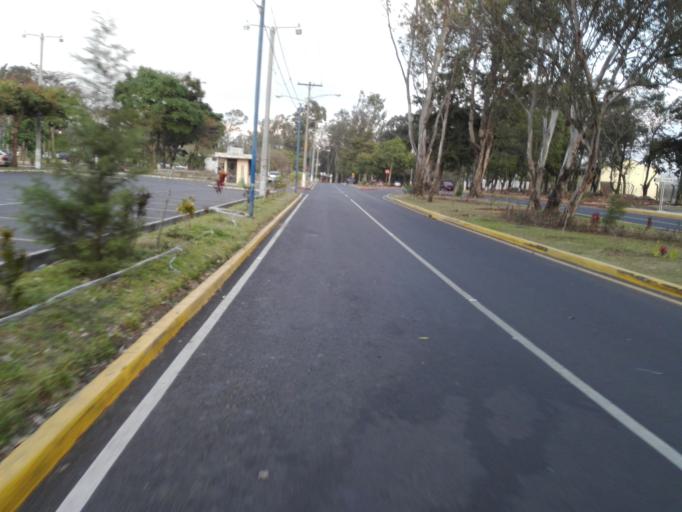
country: GT
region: Guatemala
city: Santa Catarina Pinula
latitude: 14.5818
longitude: -90.5565
